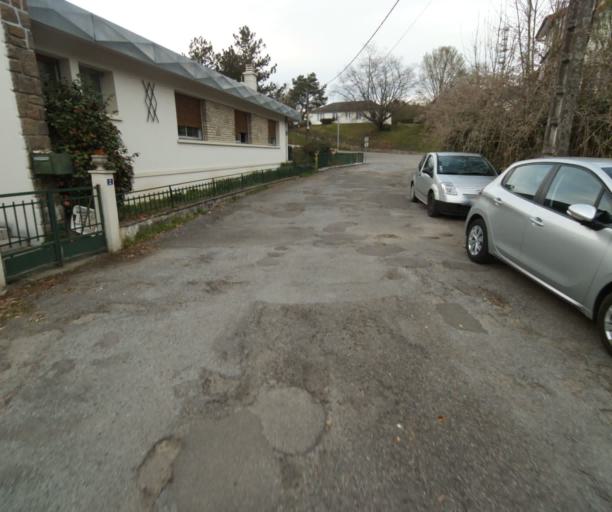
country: FR
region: Limousin
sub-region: Departement de la Correze
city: Tulle
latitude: 45.2573
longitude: 1.7648
